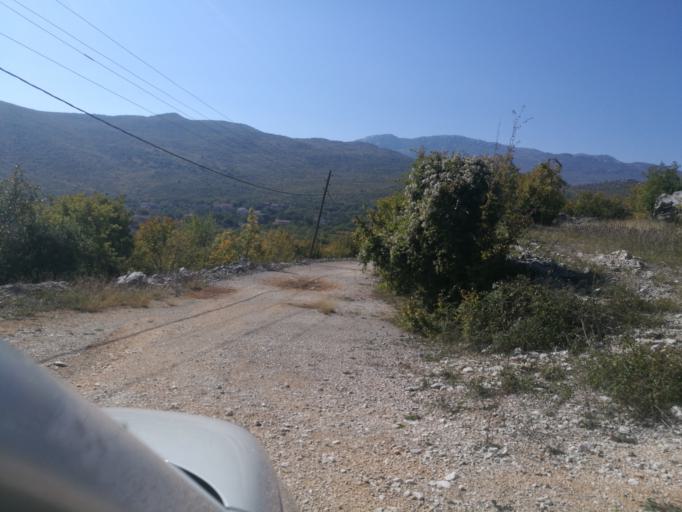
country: HR
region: Splitsko-Dalmatinska
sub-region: Grad Omis
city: Omis
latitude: 43.5193
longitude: 16.7365
